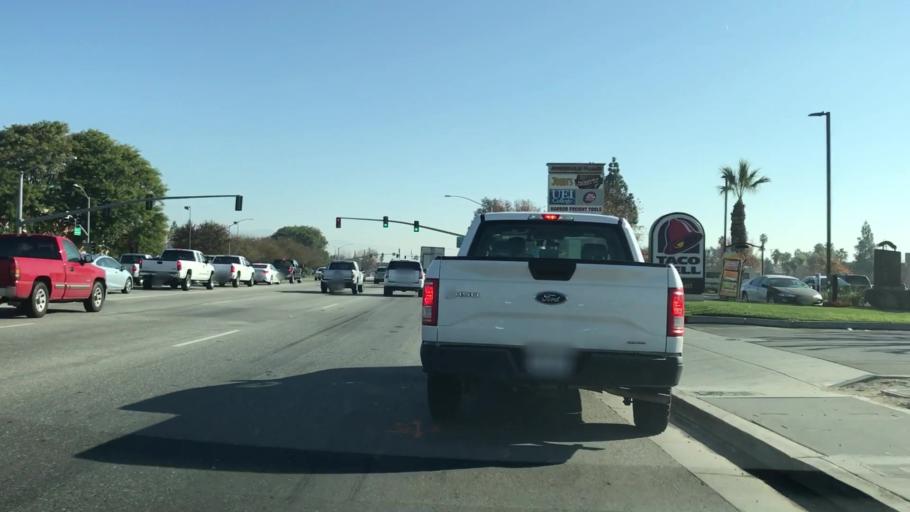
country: US
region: California
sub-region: Kern County
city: Bakersfield
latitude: 35.3831
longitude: -119.0508
